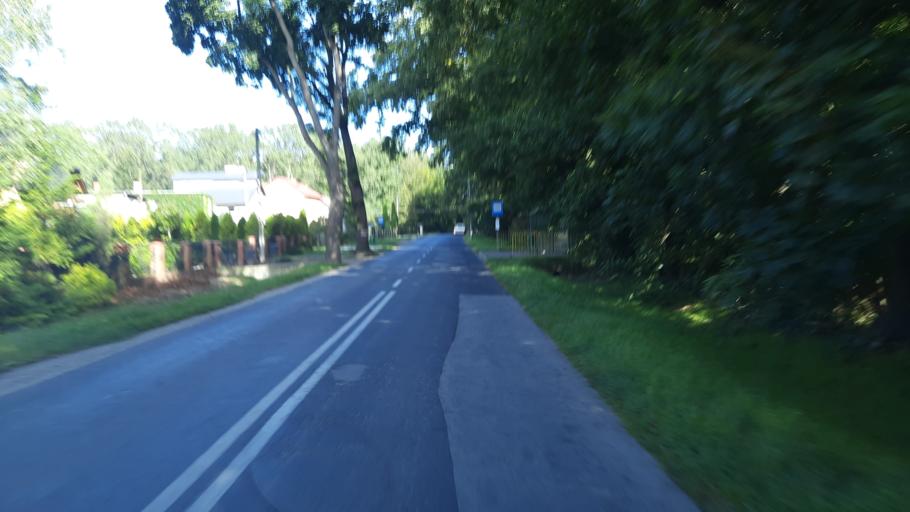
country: PL
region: Lower Silesian Voivodeship
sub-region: Powiat wroclawski
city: Dlugoleka
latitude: 51.1899
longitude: 17.1844
